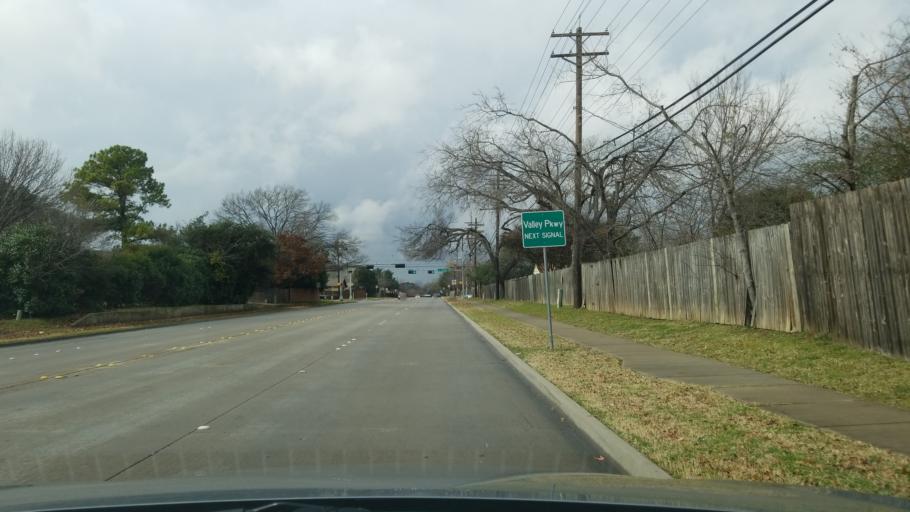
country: US
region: Texas
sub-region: Denton County
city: Lewisville
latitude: 33.0350
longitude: -97.0175
